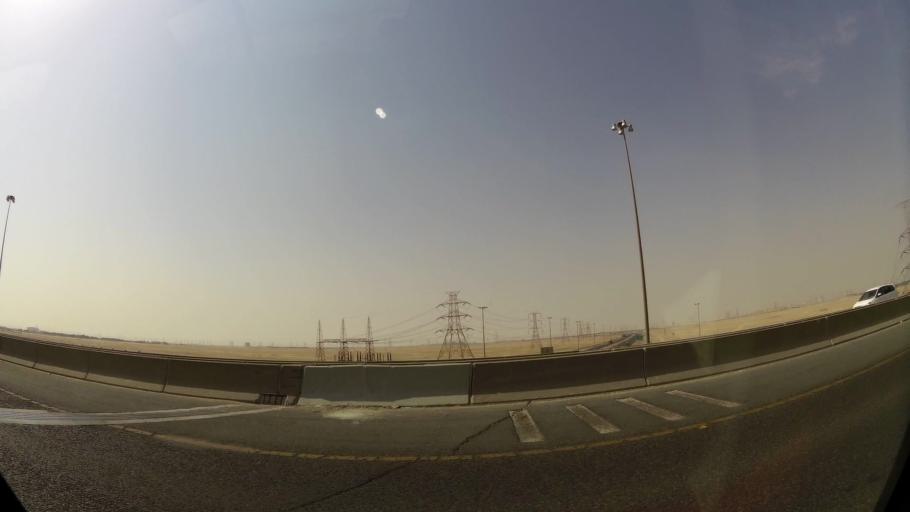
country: KW
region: Al Ahmadi
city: Al Fahahil
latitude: 29.0375
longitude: 48.1182
